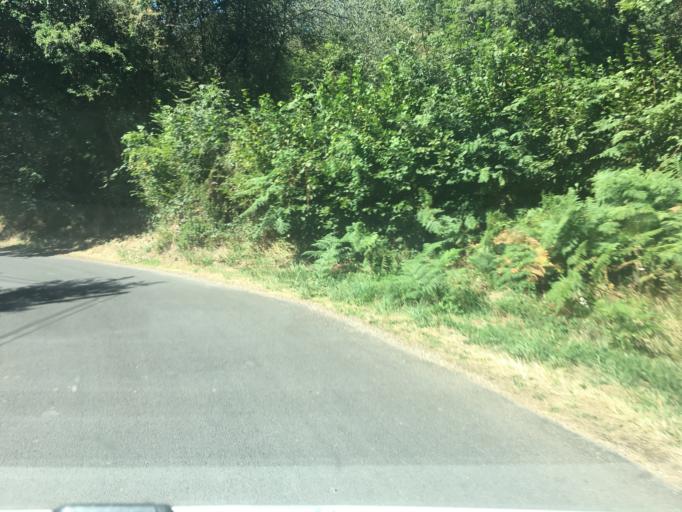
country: FR
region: Limousin
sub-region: Departement de la Correze
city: Bort-les-Orgues
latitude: 45.3986
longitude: 2.4773
